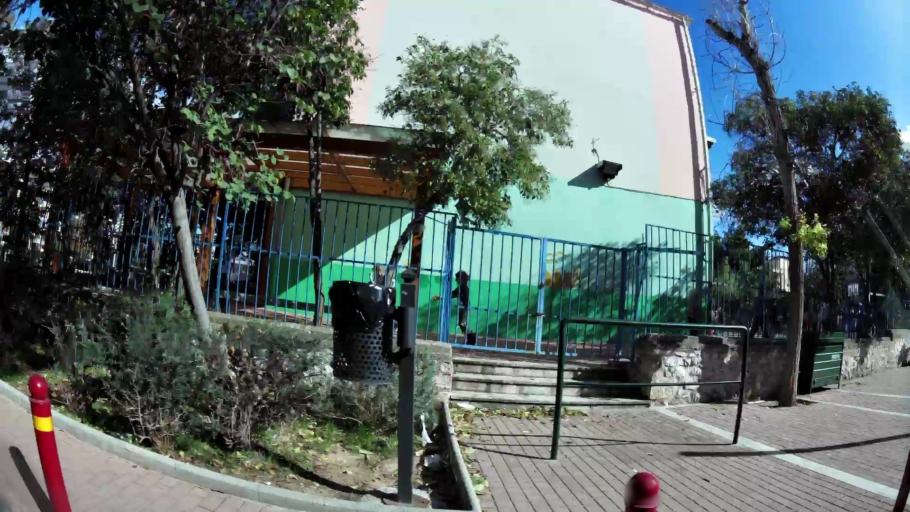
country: GR
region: Attica
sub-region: Nomarchia Athinas
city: Neo Psychiko
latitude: 38.0037
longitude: 23.7784
